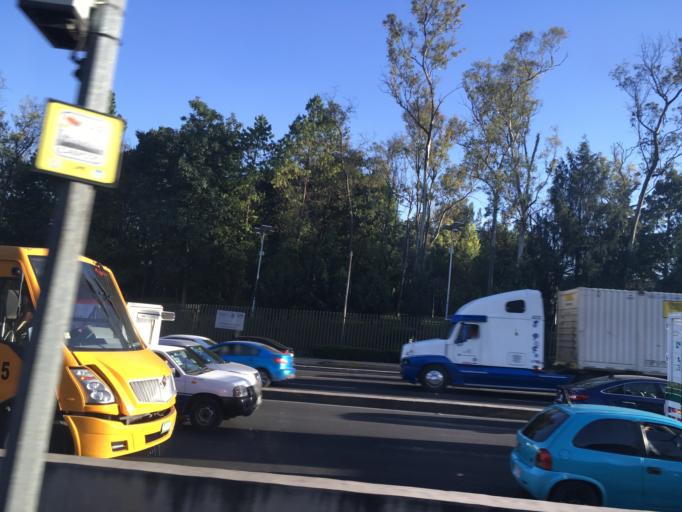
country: MX
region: Mexico City
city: Polanco
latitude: 19.3968
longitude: -99.2212
